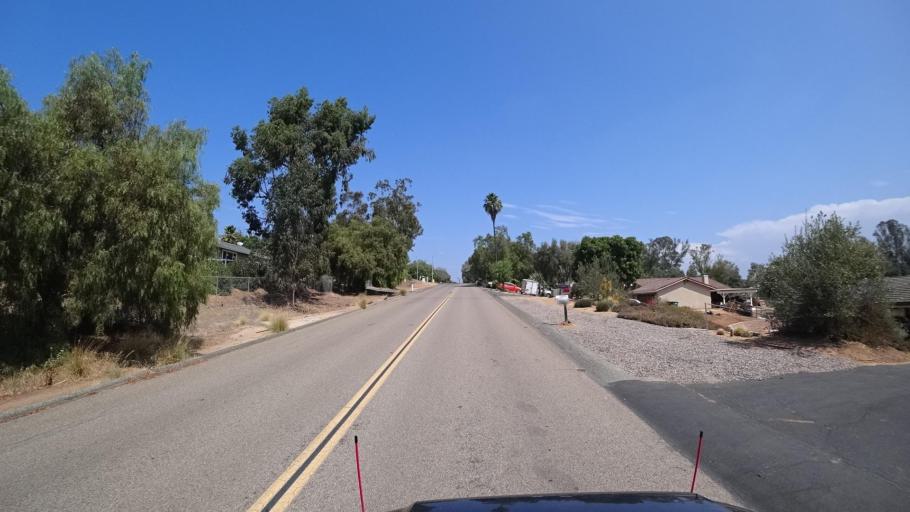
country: US
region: California
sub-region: San Diego County
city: Fallbrook
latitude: 33.3645
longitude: -117.2363
